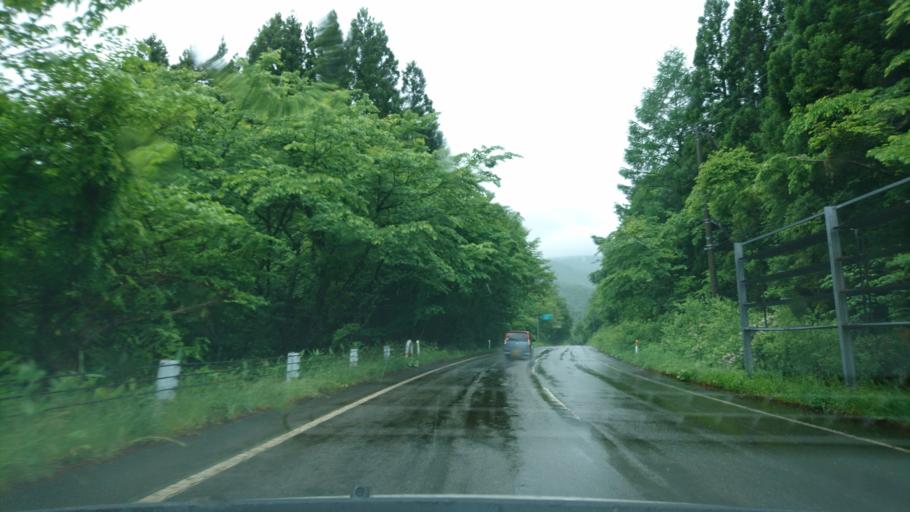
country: JP
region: Iwate
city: Ichinoseki
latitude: 39.0082
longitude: 140.8656
